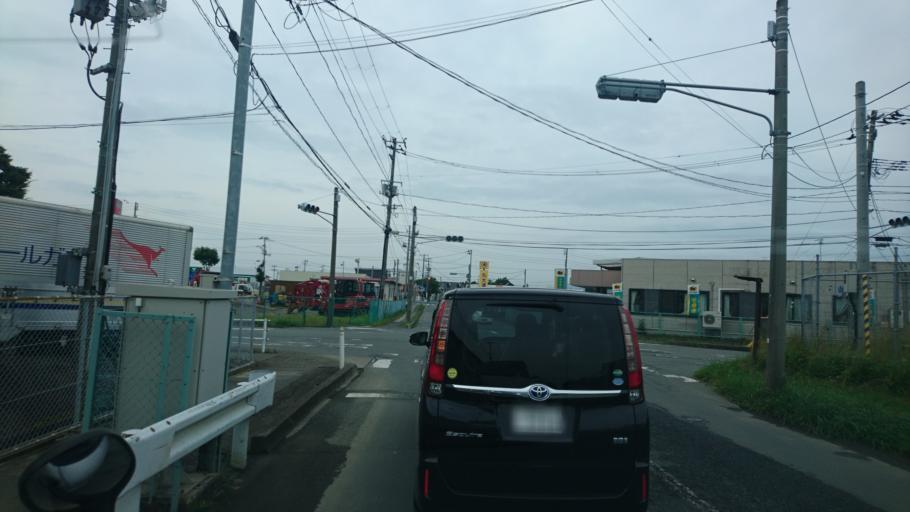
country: JP
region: Iwate
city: Morioka-shi
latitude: 39.6582
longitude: 141.1411
